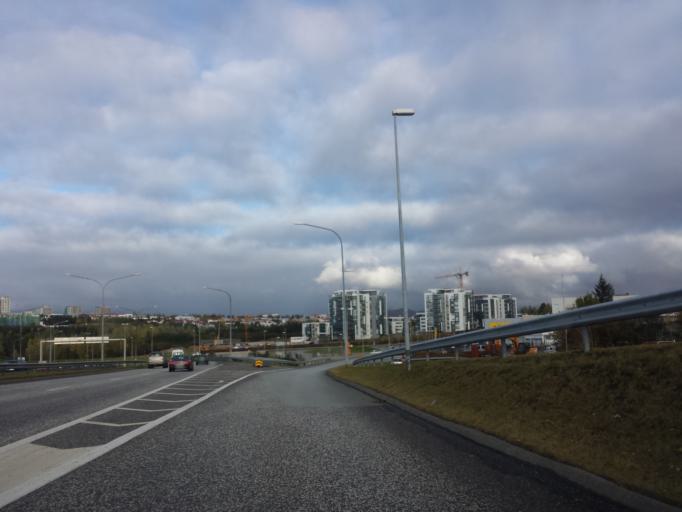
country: IS
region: Capital Region
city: Kopavogur
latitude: 64.1139
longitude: -21.9026
